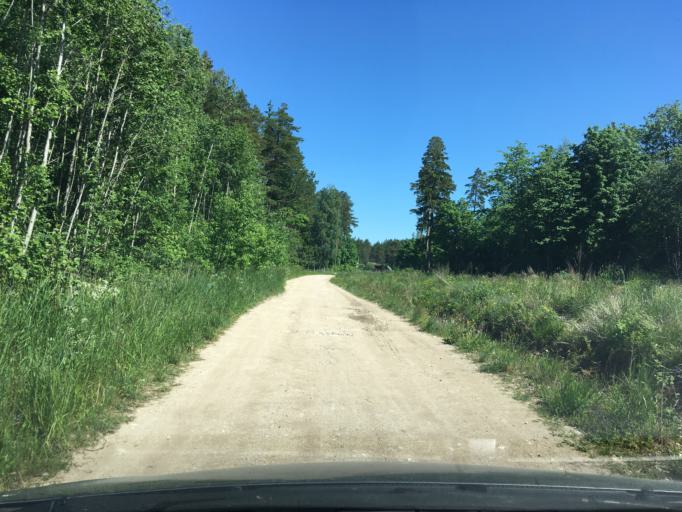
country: EE
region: Harju
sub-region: Raasiku vald
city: Raasiku
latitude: 59.1620
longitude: 25.1626
